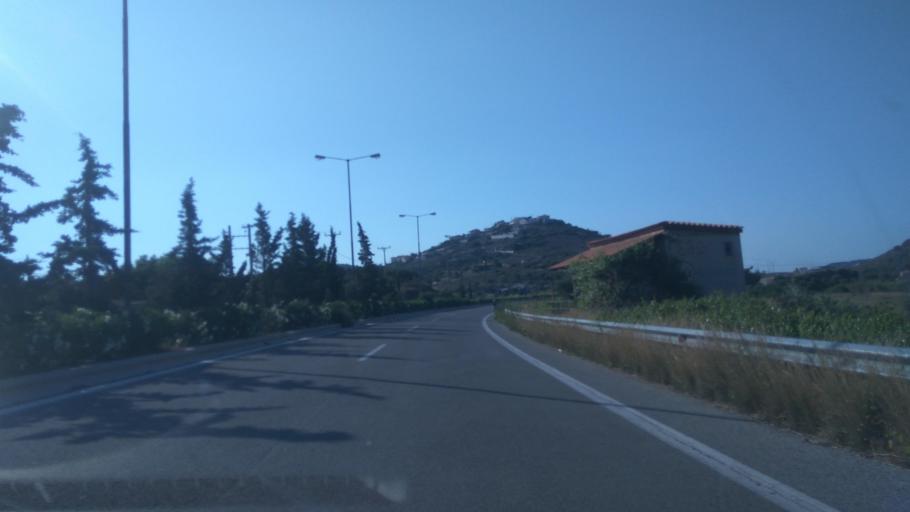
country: GR
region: Attica
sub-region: Nomarchia Anatolikis Attikis
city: Keratea
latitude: 37.8026
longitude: 24.0466
